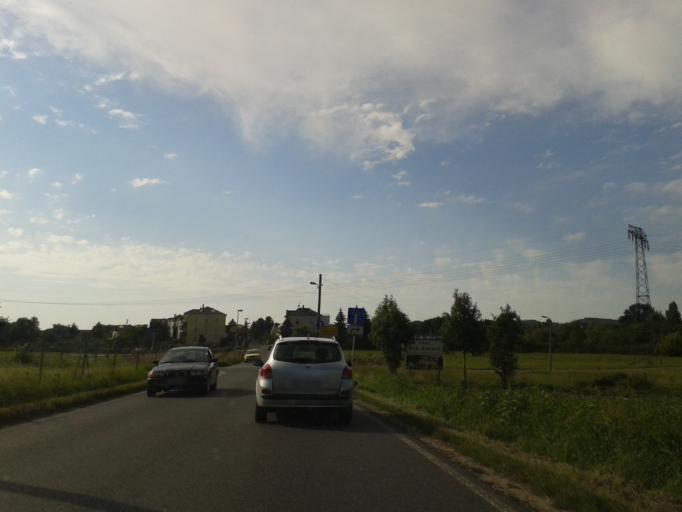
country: DE
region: Saxony
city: Radebeul
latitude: 51.0939
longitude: 13.6673
